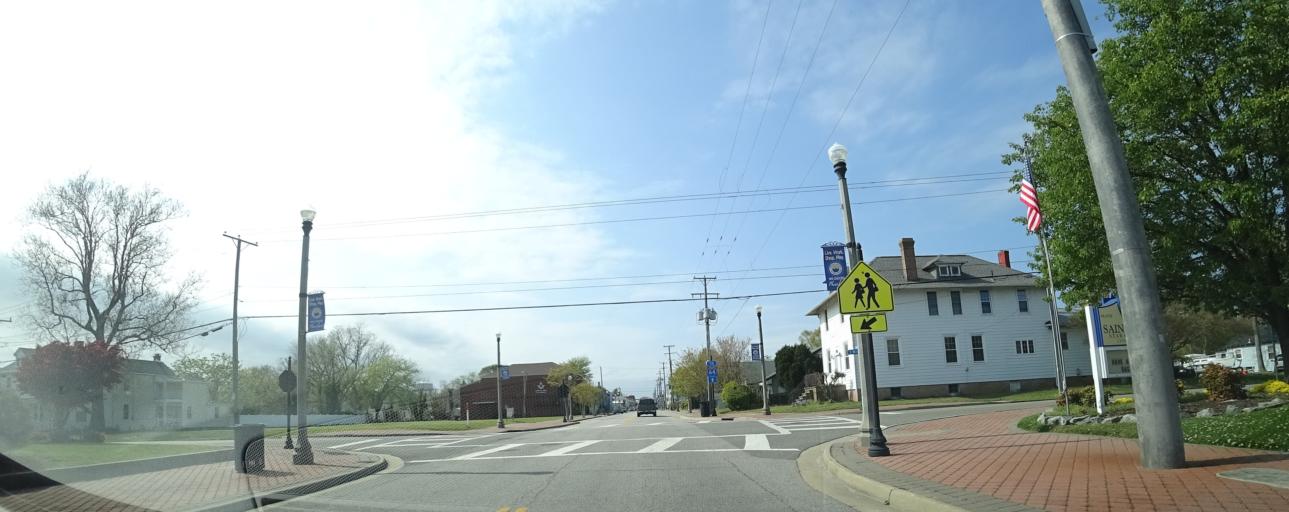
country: US
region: Virginia
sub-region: City of Hampton
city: East Hampton
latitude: 37.0155
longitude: -76.3189
